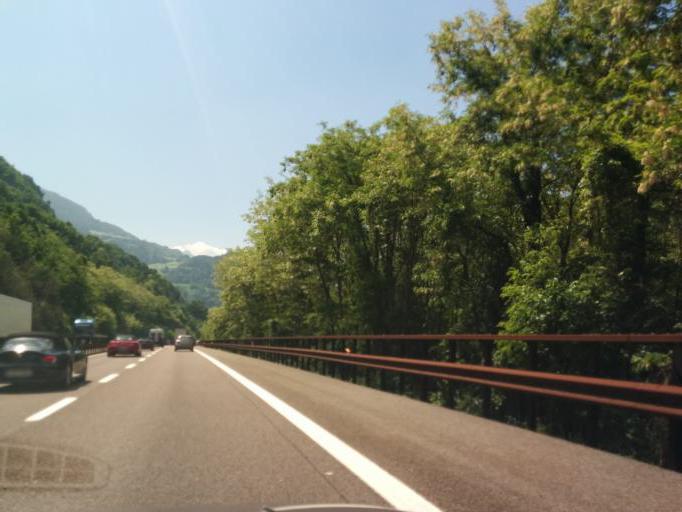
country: IT
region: Trentino-Alto Adige
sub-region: Bolzano
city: Ponte Gardena
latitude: 46.5838
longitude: 11.5243
